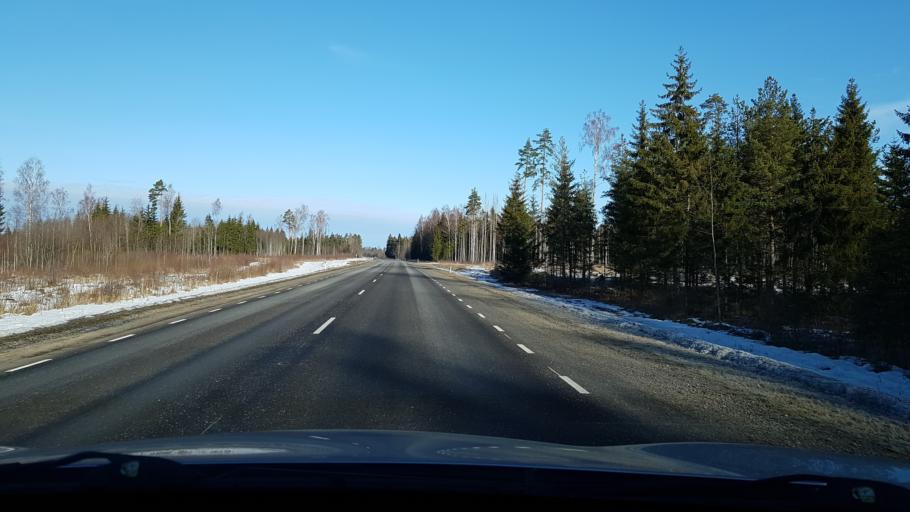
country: EE
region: Viljandimaa
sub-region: Vohma linn
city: Vohma
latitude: 58.6047
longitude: 25.5725
